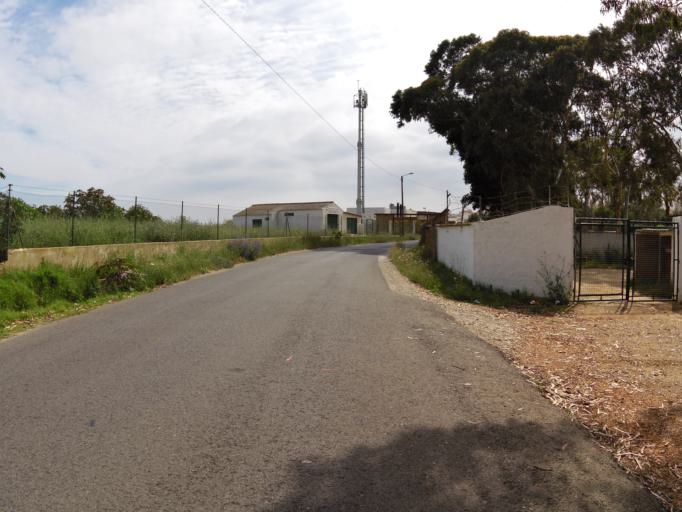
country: PT
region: Faro
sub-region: Silves
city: Armacao de Pera
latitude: 37.1077
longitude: -8.3509
